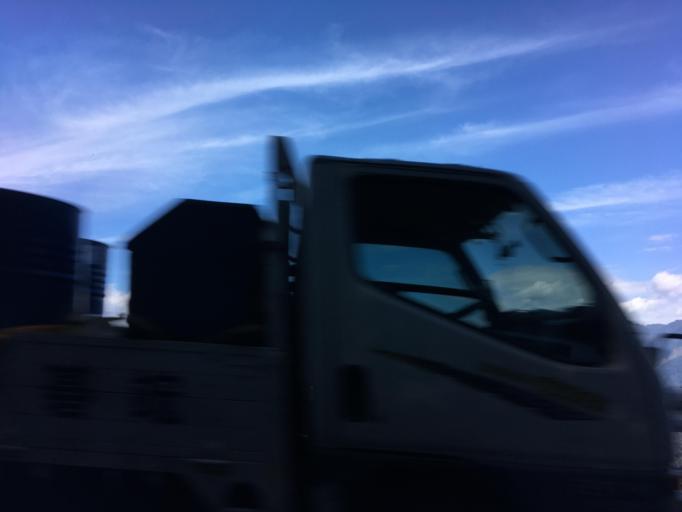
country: TW
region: Taiwan
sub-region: Yilan
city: Yilan
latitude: 24.5339
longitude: 121.5165
